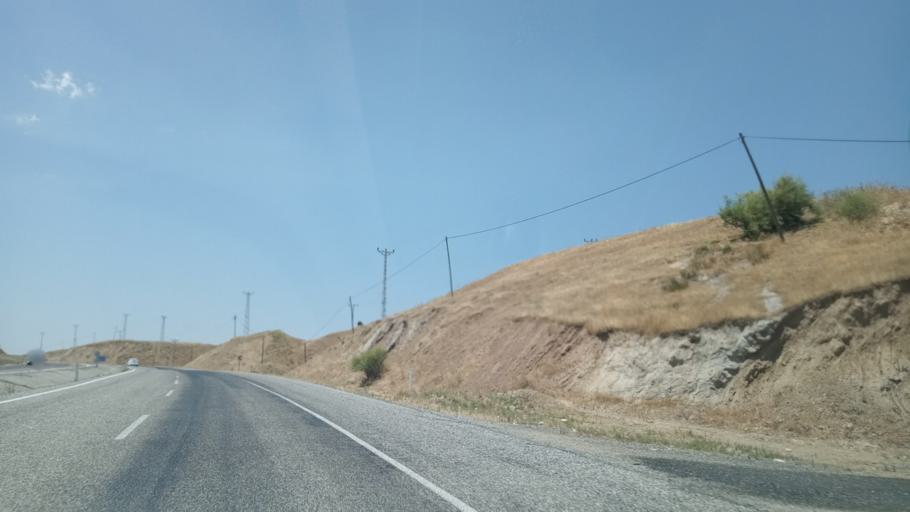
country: TR
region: Batman
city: Bekirhan
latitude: 38.1505
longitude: 41.3057
